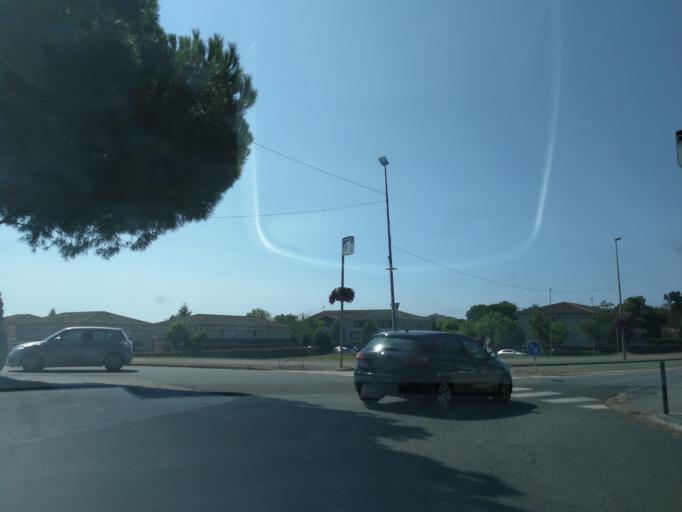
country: FR
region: Midi-Pyrenees
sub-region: Departement de la Haute-Garonne
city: Saint-Orens-de-Gameville
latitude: 43.5846
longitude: 1.5319
